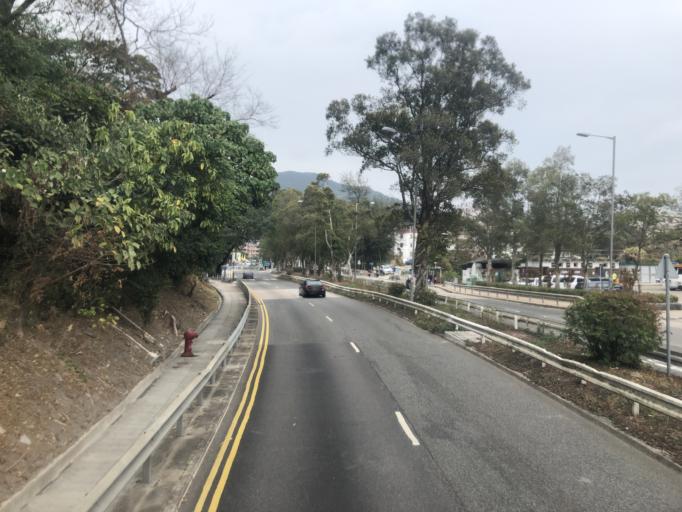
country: HK
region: Wong Tai Sin
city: Wong Tai Sin
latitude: 22.3337
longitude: 114.2361
